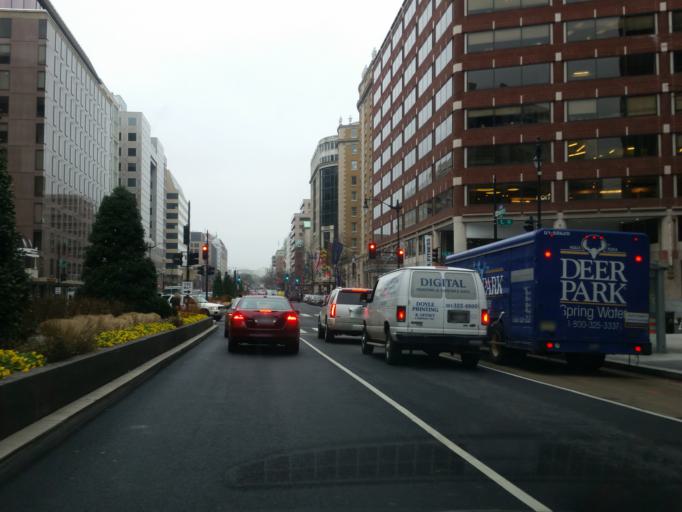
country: US
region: Washington, D.C.
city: Washington, D.C.
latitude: 38.9033
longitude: -77.0398
